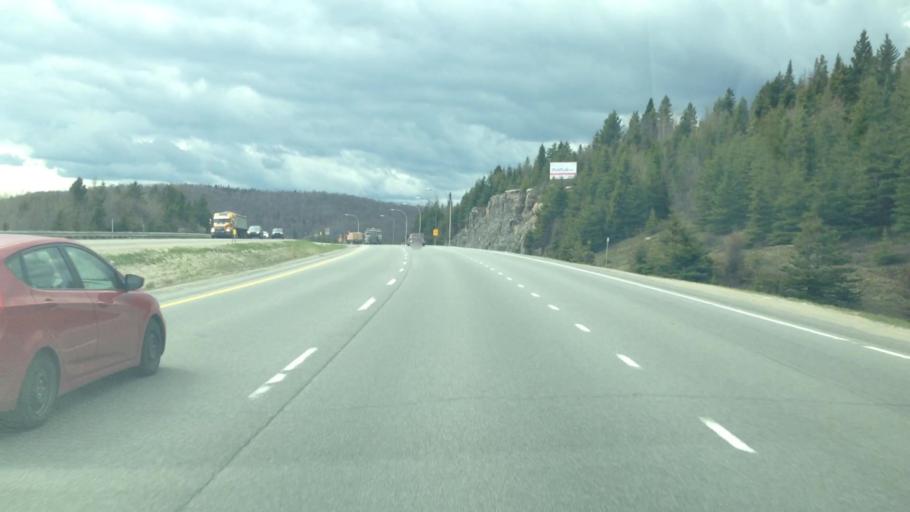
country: CA
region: Quebec
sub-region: Laurentides
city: Val-David
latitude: 45.9886
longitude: -74.1893
